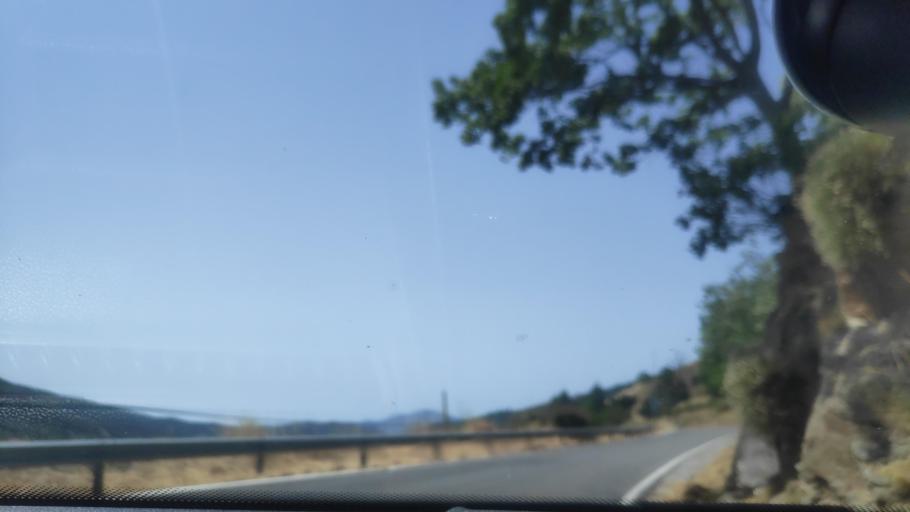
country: ES
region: Andalusia
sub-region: Provincia de Granada
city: Trevelez
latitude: 36.9873
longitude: -3.2716
